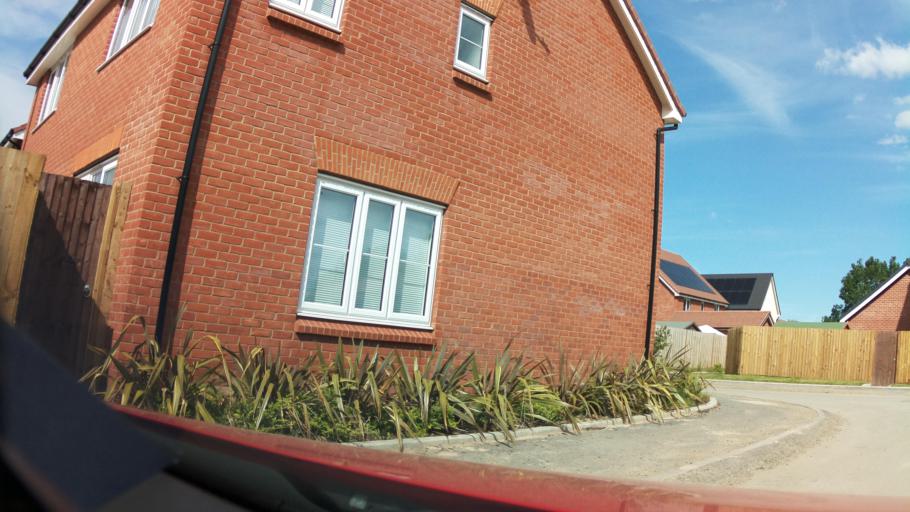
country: GB
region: England
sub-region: Worcestershire
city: Pershore
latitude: 52.1333
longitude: -2.1119
